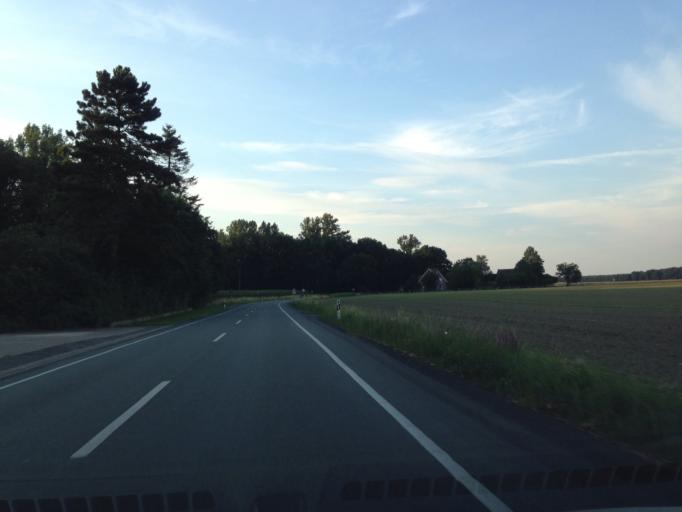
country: DE
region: North Rhine-Westphalia
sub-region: Regierungsbezirk Munster
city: Senden
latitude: 51.8554
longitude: 7.5471
